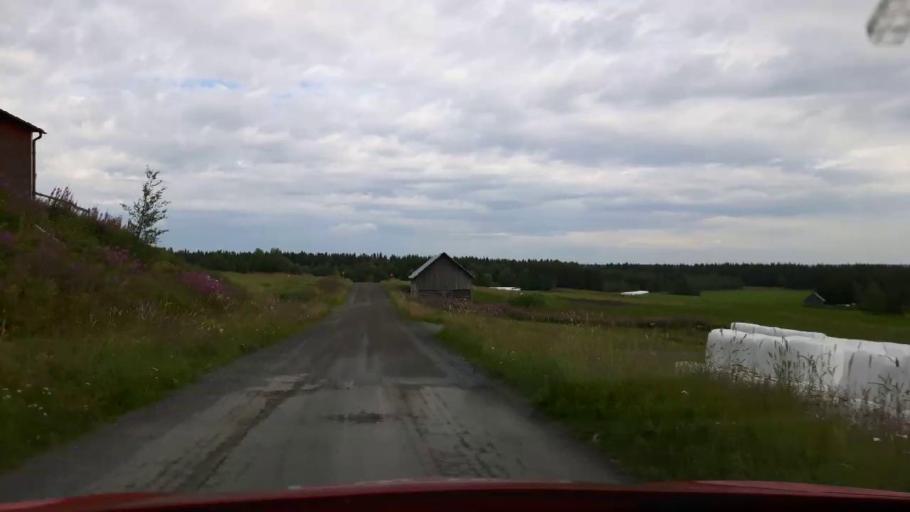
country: SE
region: Jaemtland
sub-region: OEstersunds Kommun
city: Lit
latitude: 63.3801
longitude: 15.1942
